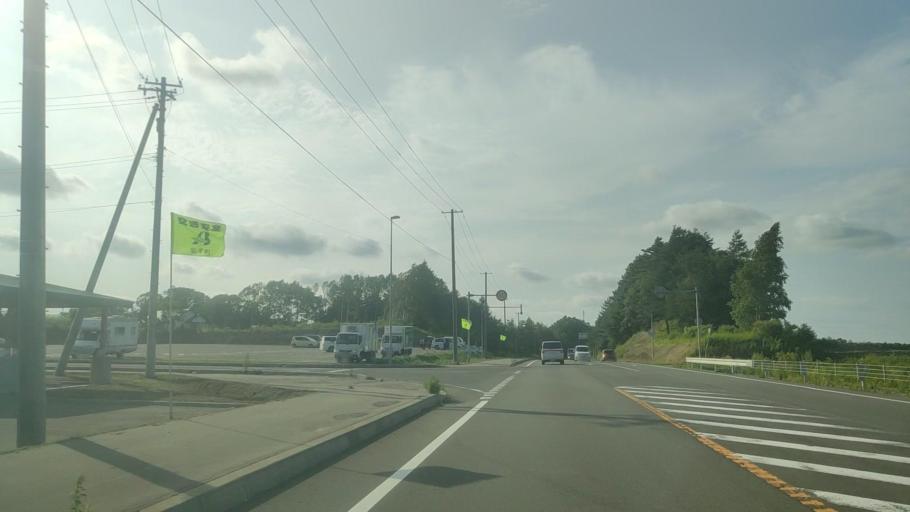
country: JP
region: Hokkaido
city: Chitose
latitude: 42.8765
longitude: 141.8190
